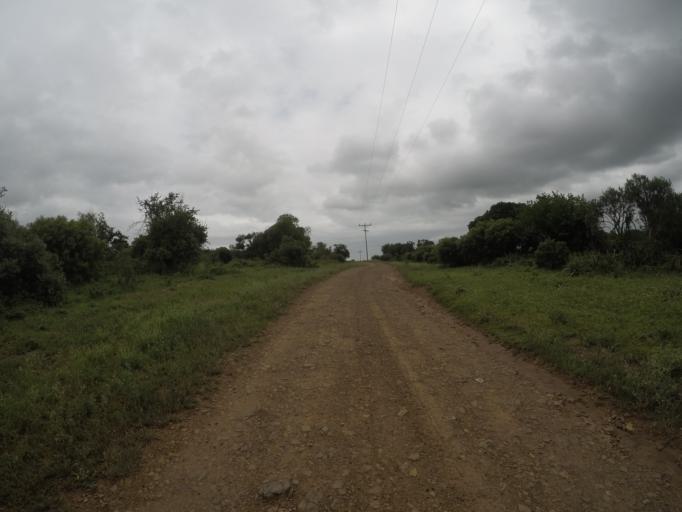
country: ZA
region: KwaZulu-Natal
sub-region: uThungulu District Municipality
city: Empangeni
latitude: -28.5969
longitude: 31.8315
